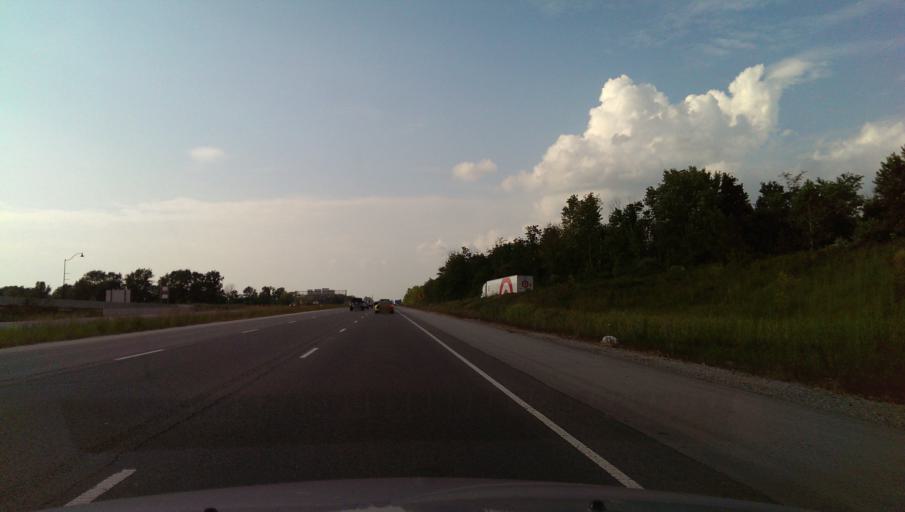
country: US
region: Indiana
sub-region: Hamilton County
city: Westfield
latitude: 40.0222
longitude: -86.1316
